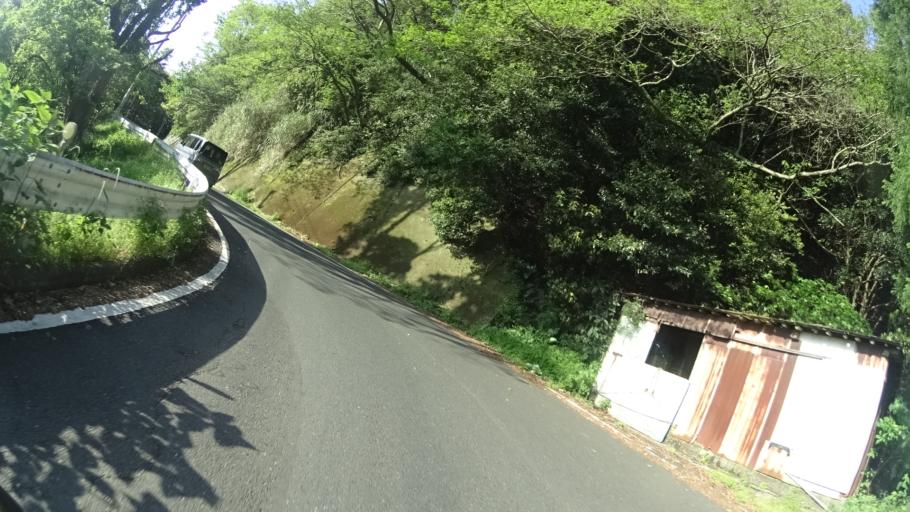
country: JP
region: Ehime
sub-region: Nishiuwa-gun
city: Ikata-cho
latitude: 33.3867
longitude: 132.0884
